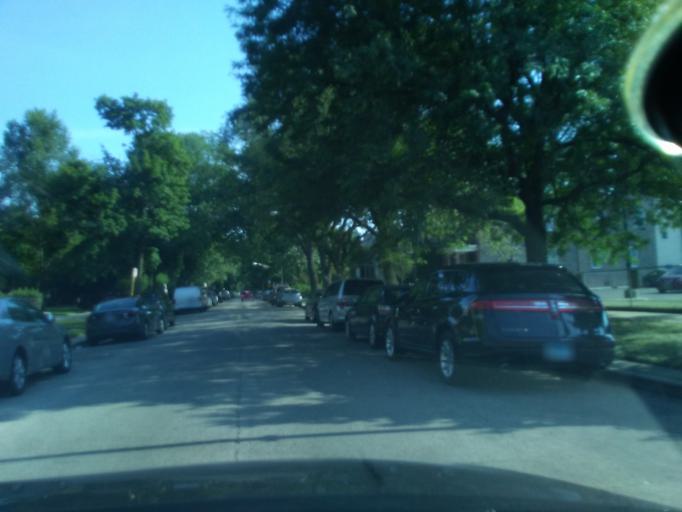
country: US
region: Illinois
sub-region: Cook County
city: Lincolnwood
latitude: 41.9728
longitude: -87.6711
